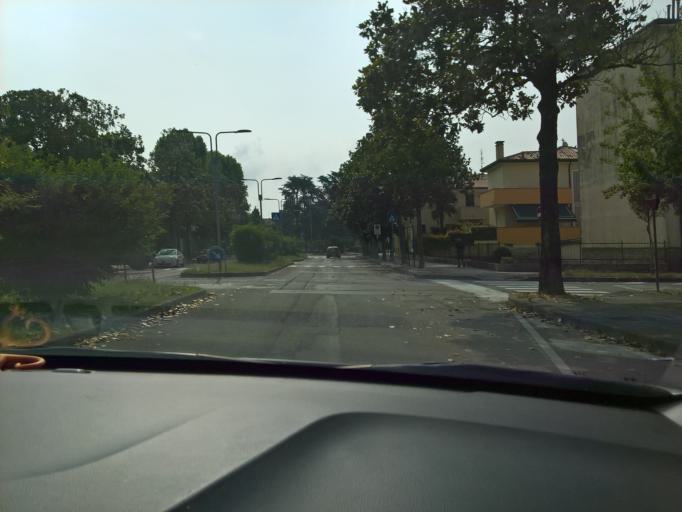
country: IT
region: Veneto
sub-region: Provincia di Padova
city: Battaglia Terme
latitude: 45.2906
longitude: 11.7822
